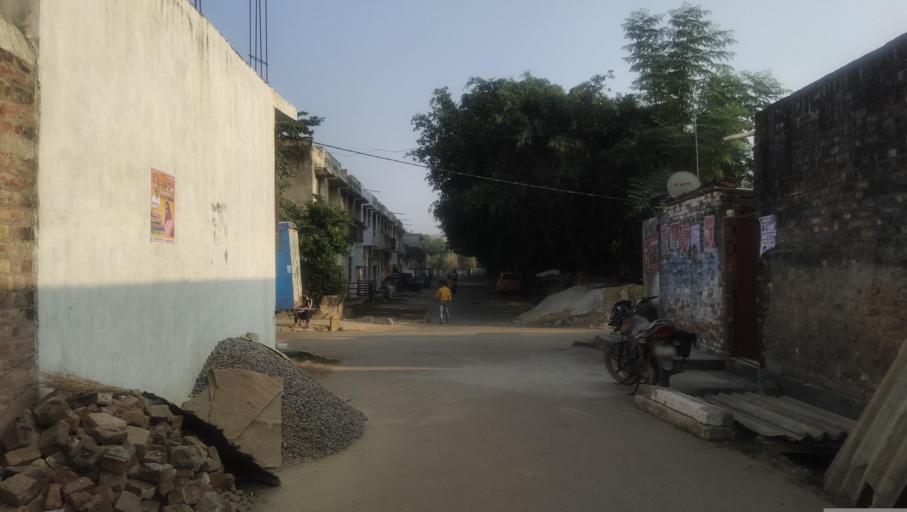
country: IN
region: Uttar Pradesh
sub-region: Lucknow District
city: Goshainganj
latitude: 26.7902
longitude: 81.0123
